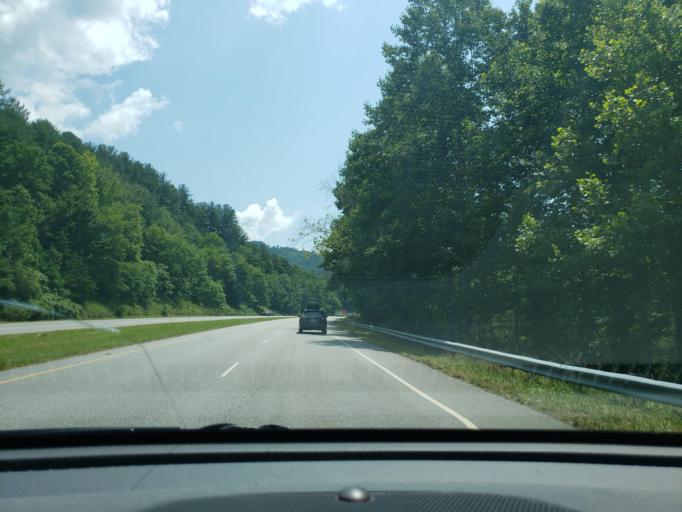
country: US
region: North Carolina
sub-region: Wilkes County
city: Millers Creek
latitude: 36.1808
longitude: -81.3901
